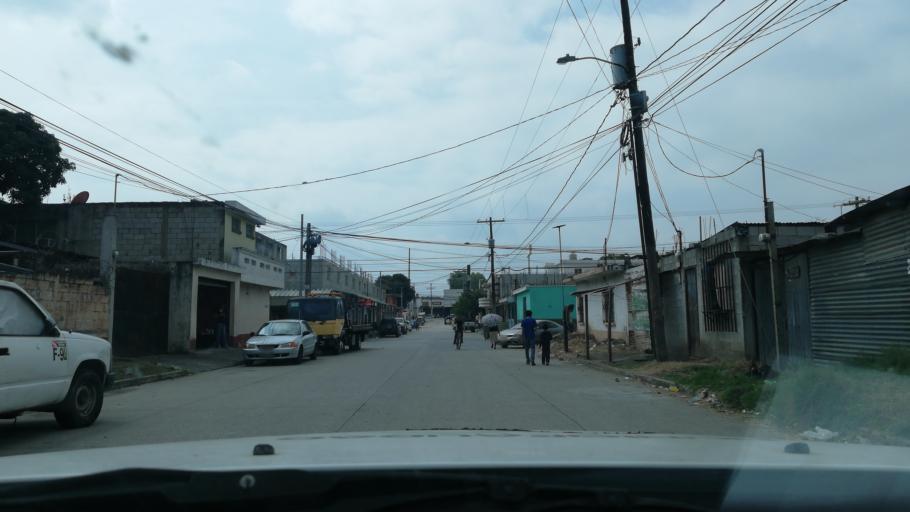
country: GT
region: Guatemala
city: Petapa
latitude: 14.5060
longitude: -90.5656
